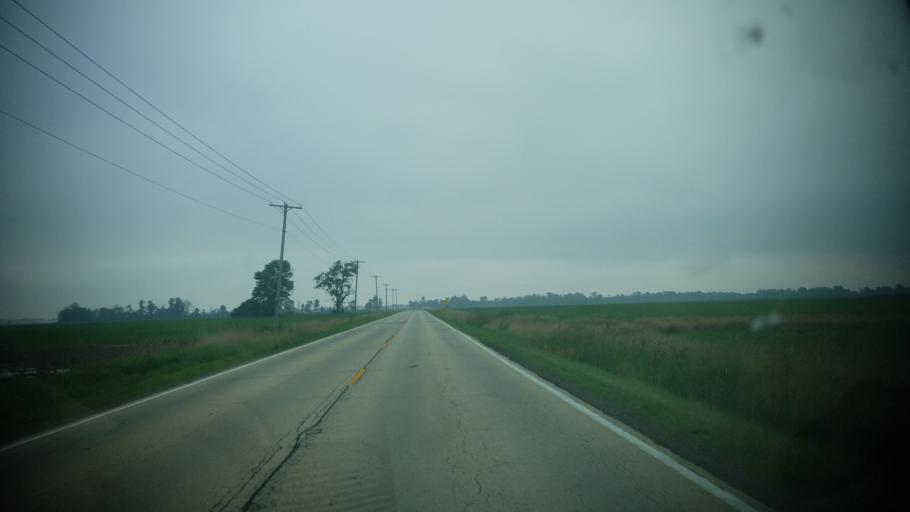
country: US
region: Illinois
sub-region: Clay County
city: Flora
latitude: 38.6432
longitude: -88.4380
